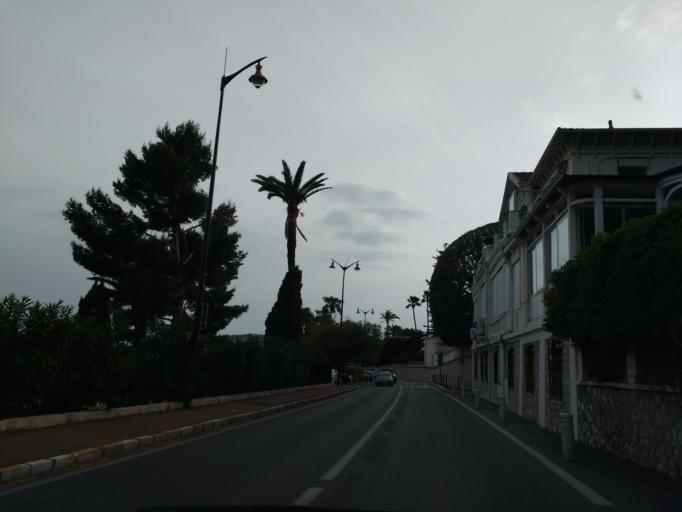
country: FR
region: Provence-Alpes-Cote d'Azur
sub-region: Departement des Alpes-Maritimes
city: Beaulieu-sur-Mer
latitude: 43.7118
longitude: 7.3362
